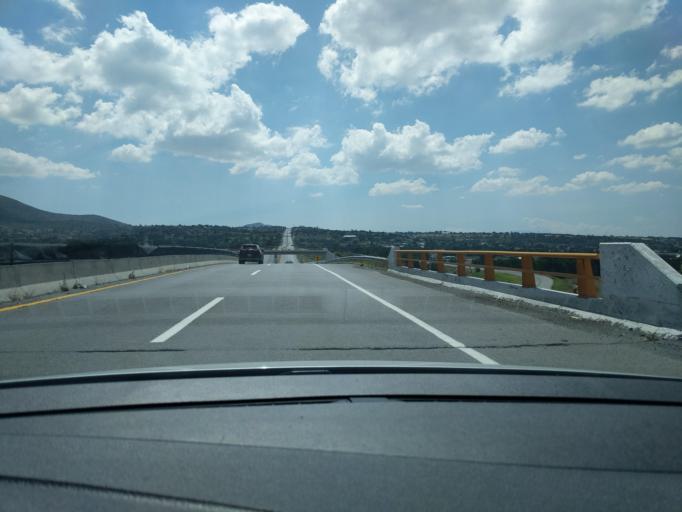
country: MX
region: Hidalgo
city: Zempoala
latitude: 19.8813
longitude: -98.6652
